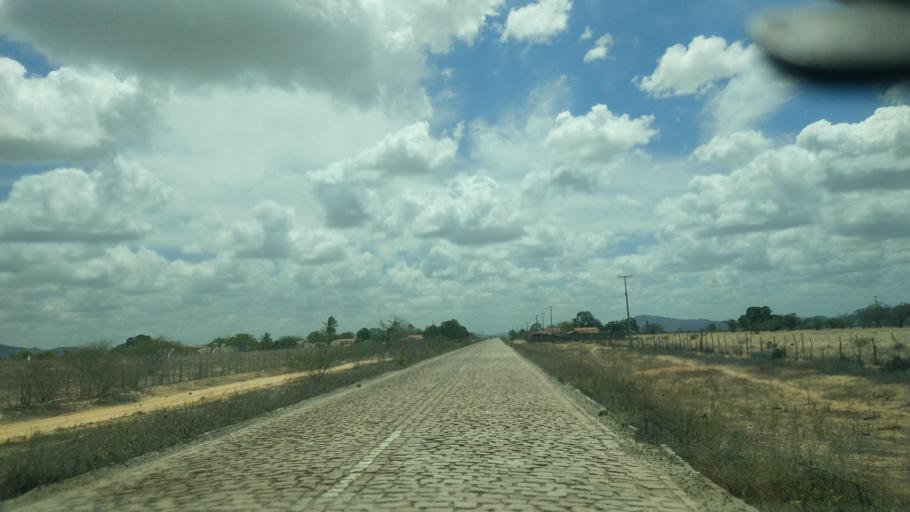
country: BR
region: Rio Grande do Norte
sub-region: Sao Paulo Do Potengi
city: Sao Paulo do Potengi
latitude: -5.9778
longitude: -35.8565
